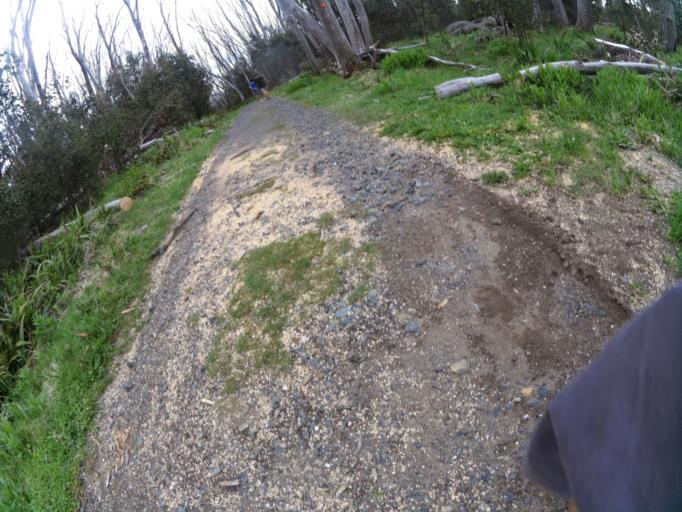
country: AU
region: Victoria
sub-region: Yarra Ranges
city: Millgrove
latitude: -37.4999
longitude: 145.8785
